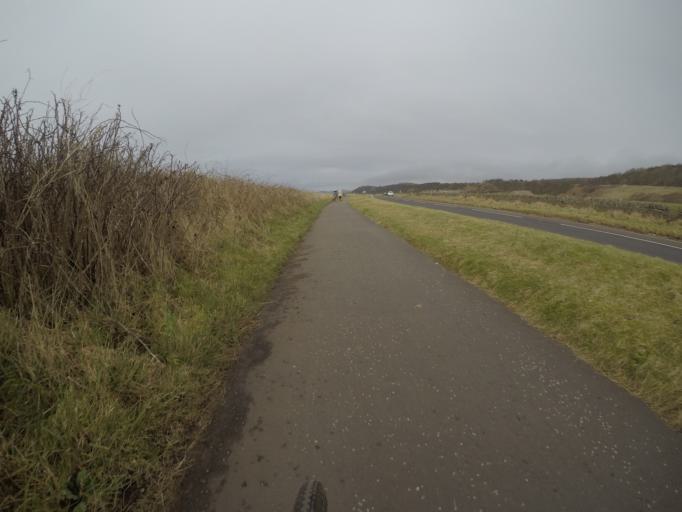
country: GB
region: Scotland
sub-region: North Ayrshire
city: Ardrossan
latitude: 55.6572
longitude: -4.8290
